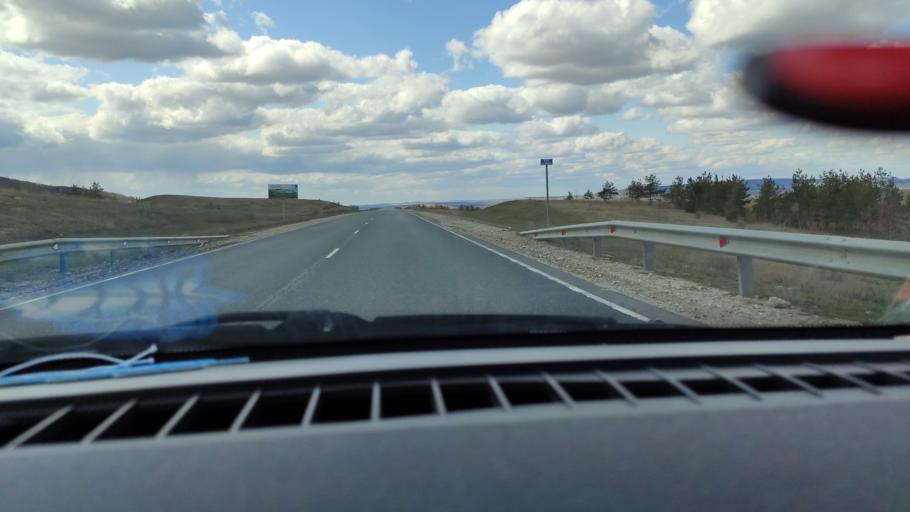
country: RU
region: Saratov
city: Alekseyevka
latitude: 52.3559
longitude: 47.9461
